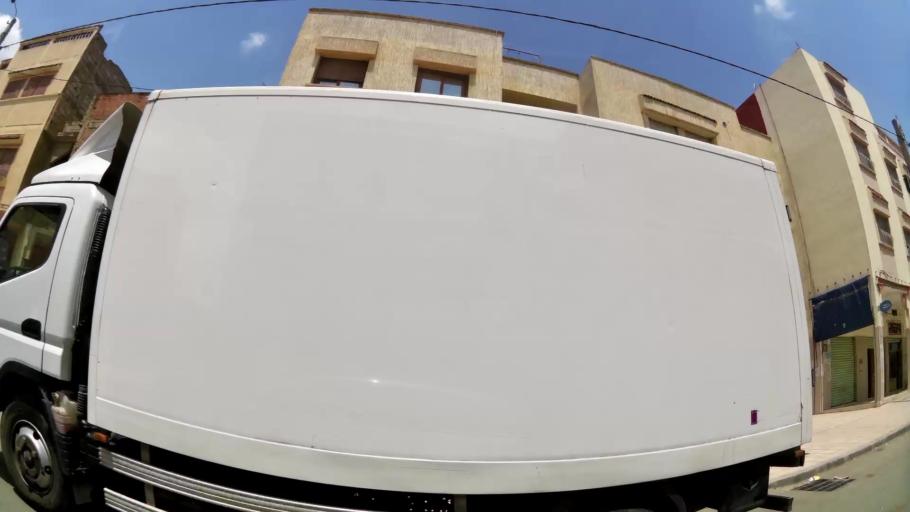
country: MA
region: Rabat-Sale-Zemmour-Zaer
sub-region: Khemisset
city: Tiflet
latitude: 34.0080
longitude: -6.5310
